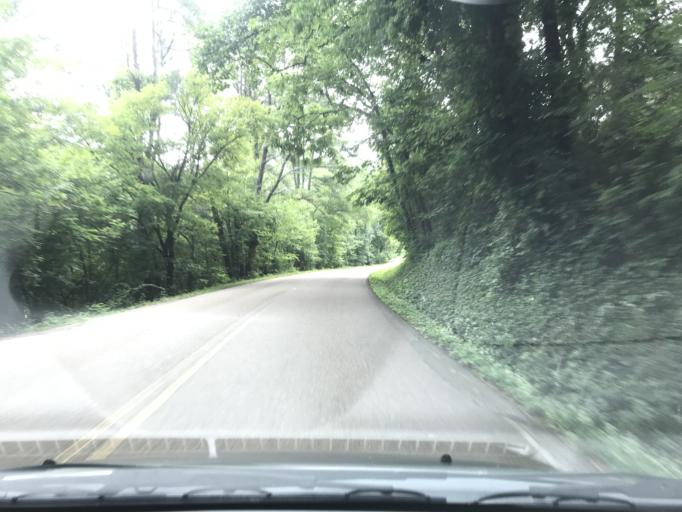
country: US
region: Tennessee
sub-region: Hamilton County
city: Lakesite
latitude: 35.2065
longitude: -85.0923
